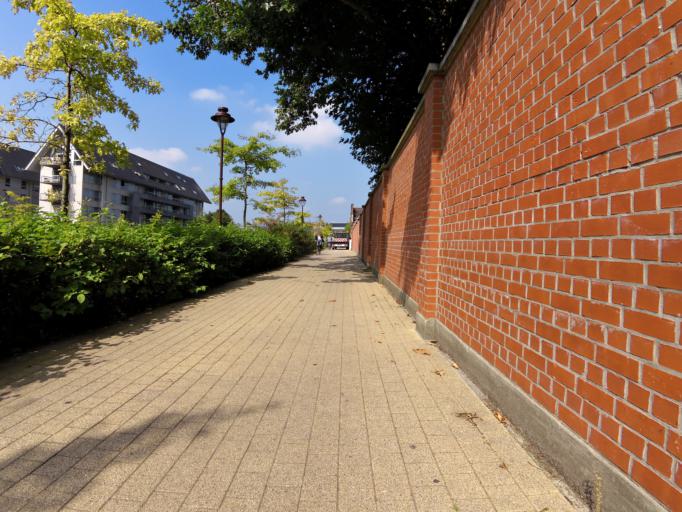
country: BE
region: Flanders
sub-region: Provincie West-Vlaanderen
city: Roeselare
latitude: 50.9512
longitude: 3.1263
